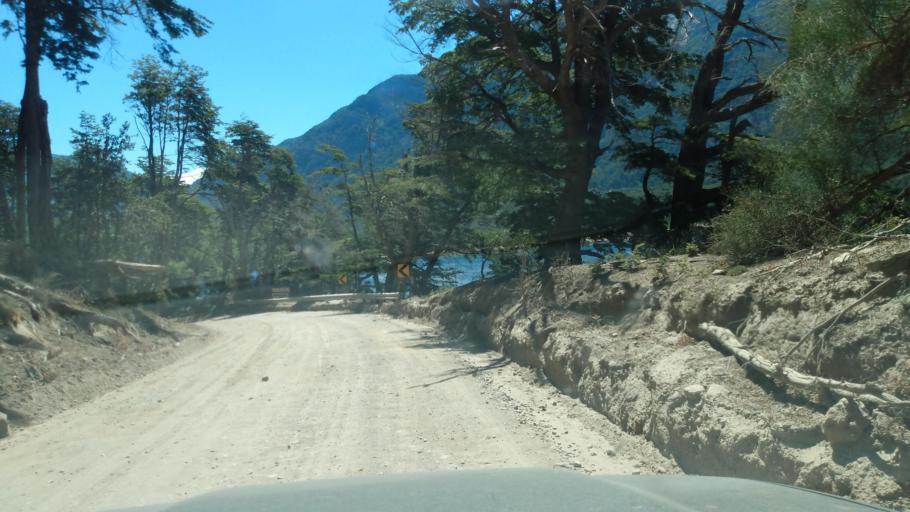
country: AR
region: Neuquen
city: Villa La Angostura
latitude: -40.6159
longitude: -71.5400
